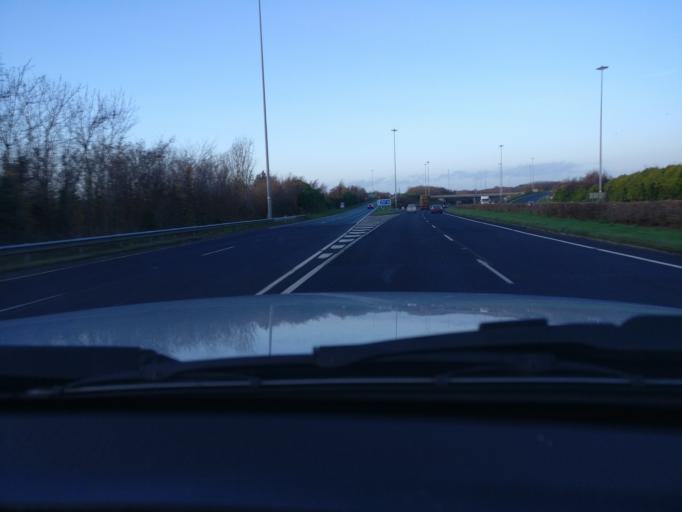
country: IE
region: Leinster
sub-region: Lu
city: Dundalk
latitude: 53.9658
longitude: -6.4227
